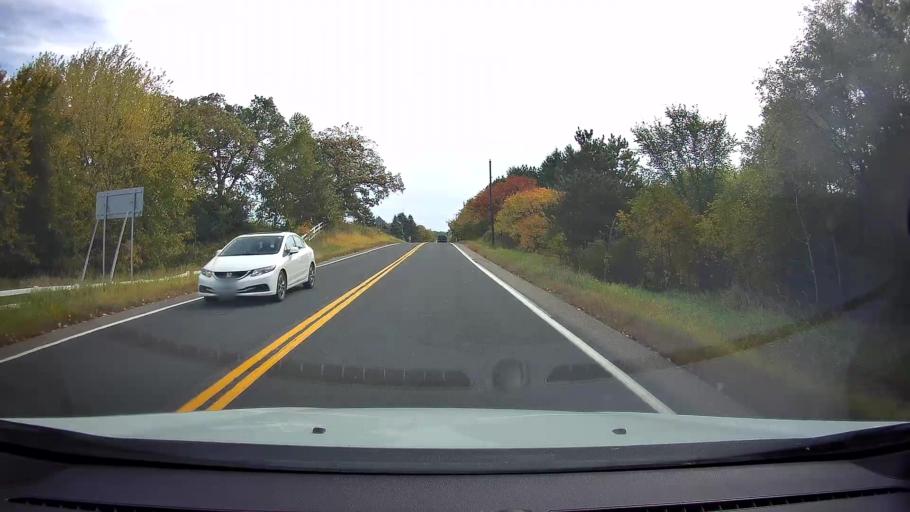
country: US
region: Minnesota
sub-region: Washington County
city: Grant
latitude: 45.0846
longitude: -92.9227
